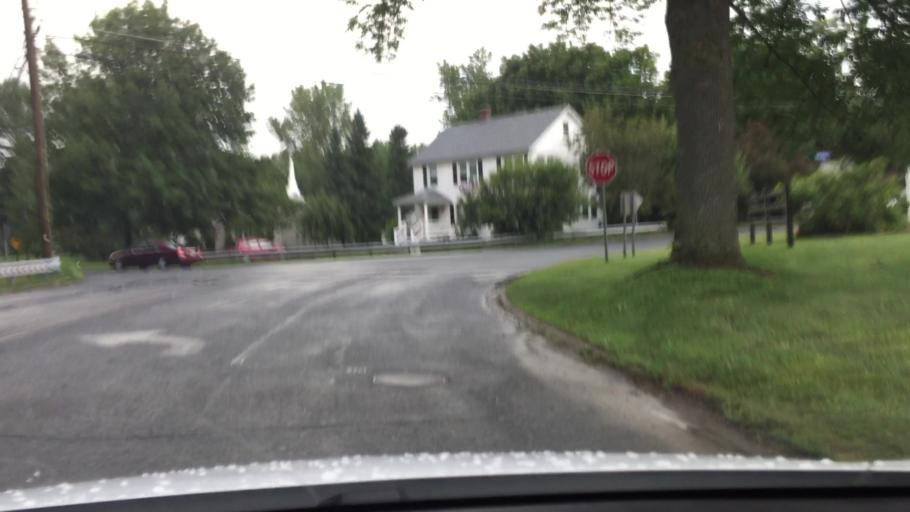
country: US
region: Massachusetts
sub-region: Berkshire County
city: Pittsfield
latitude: 42.4296
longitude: -73.1971
